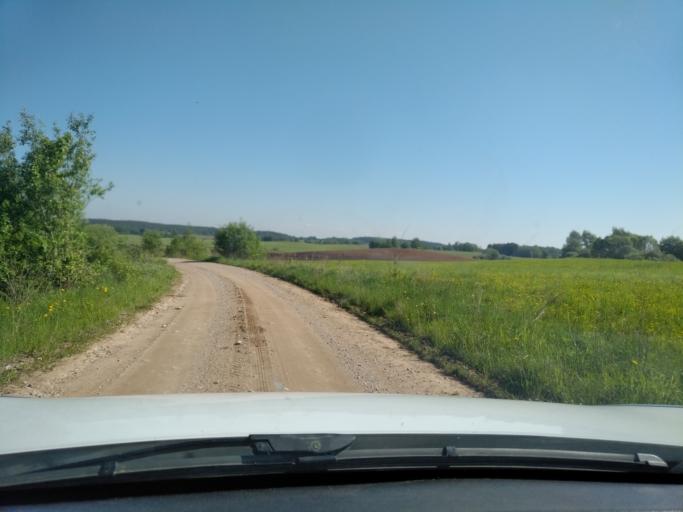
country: LT
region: Panevezys
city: Rokiskis
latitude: 55.7501
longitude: 25.6099
